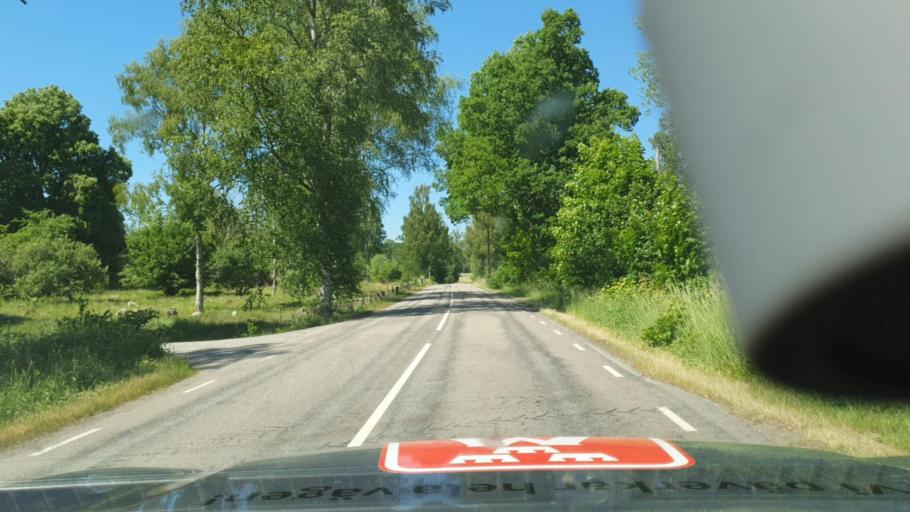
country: SE
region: Kalmar
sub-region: Torsas Kommun
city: Torsas
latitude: 56.4532
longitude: 15.8172
